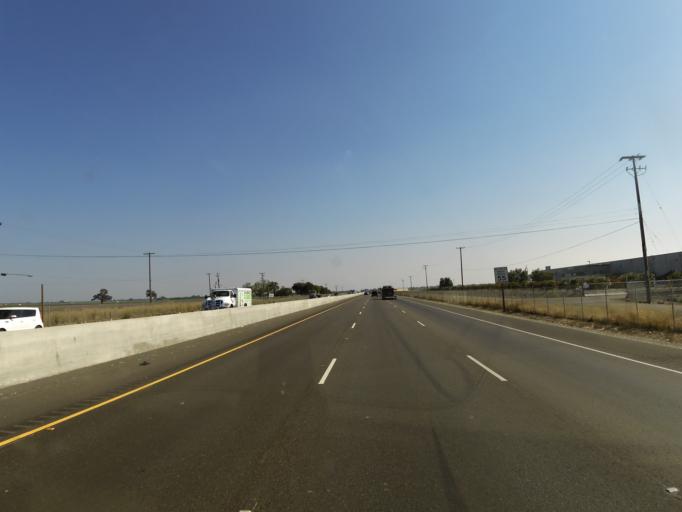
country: US
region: California
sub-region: San Joaquin County
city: Kennedy
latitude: 37.8923
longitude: -121.2205
